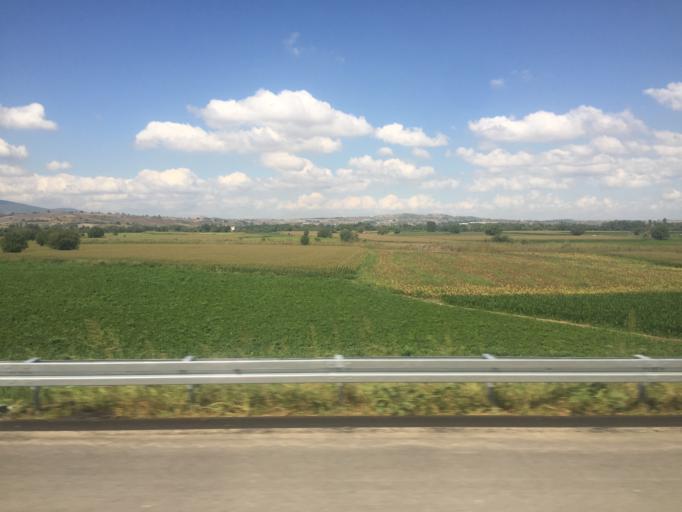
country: TR
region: Balikesir
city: Gobel
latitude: 40.0064
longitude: 28.1955
